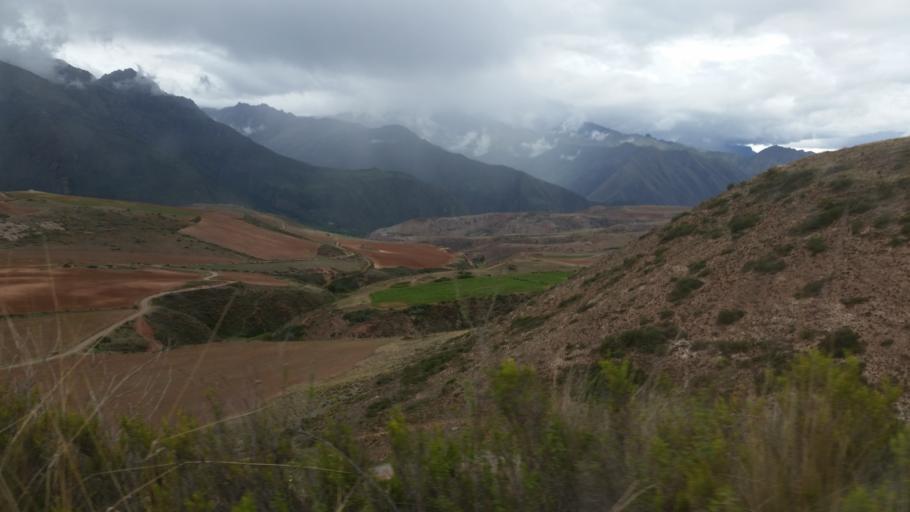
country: PE
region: Cusco
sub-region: Provincia de Urubamba
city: Maras
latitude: -13.3138
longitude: -72.1907
